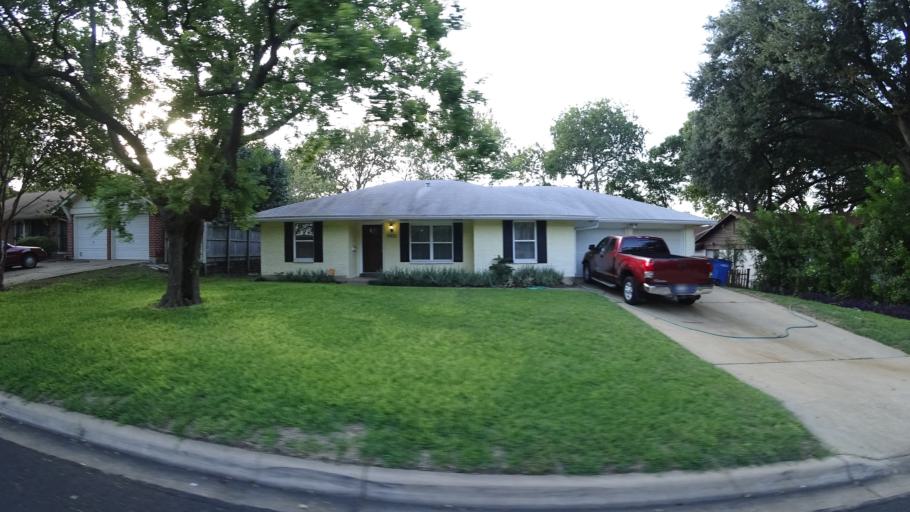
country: US
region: Texas
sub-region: Travis County
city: Wells Branch
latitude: 30.3621
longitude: -97.7052
